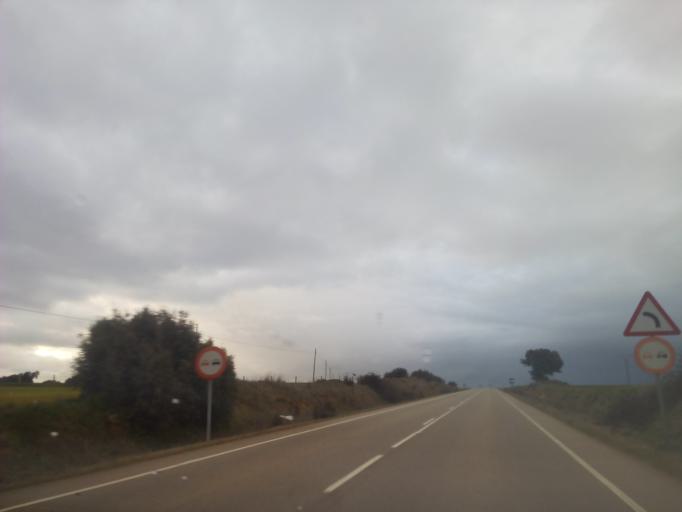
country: ES
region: Castille and Leon
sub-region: Provincia de Salamanca
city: Cabrillas
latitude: 40.7526
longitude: -6.1863
